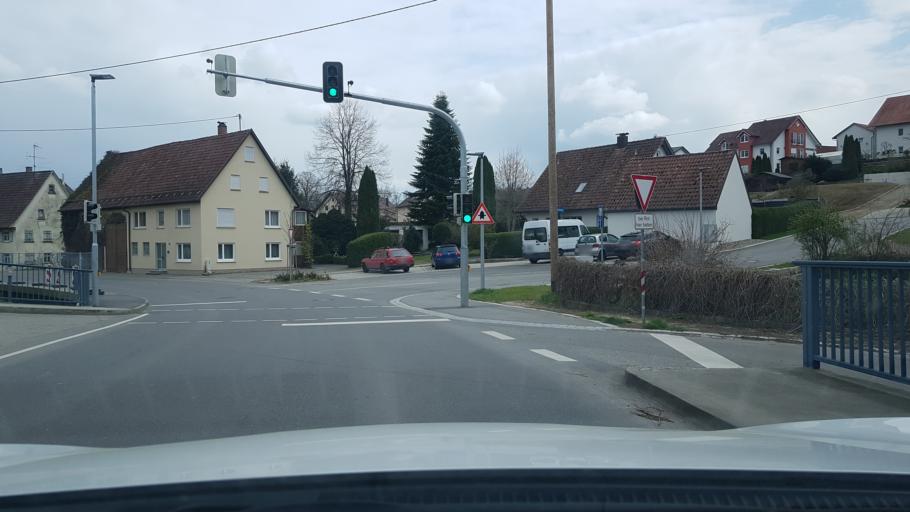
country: DE
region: Baden-Wuerttemberg
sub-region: Tuebingen Region
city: Warthausen
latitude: 48.1732
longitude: 9.7974
